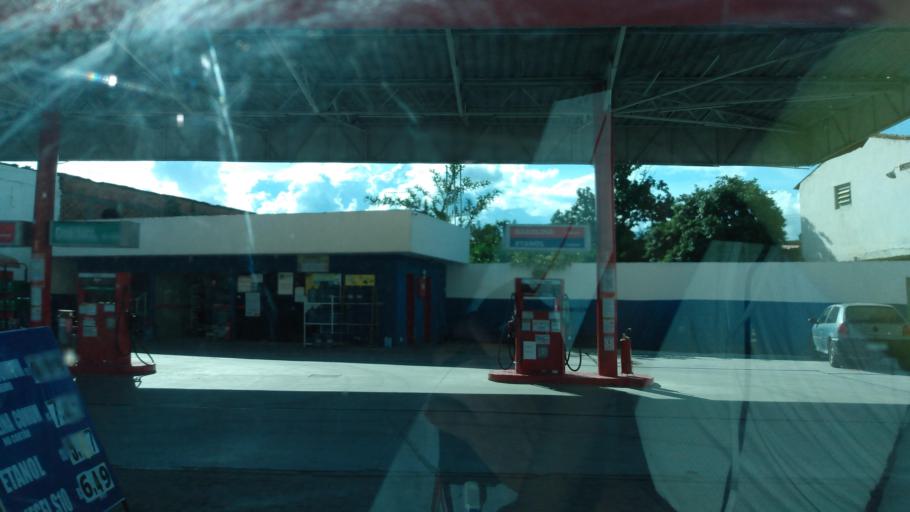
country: ET
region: Oromiya
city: Gore
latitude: 8.1983
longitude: 35.5615
